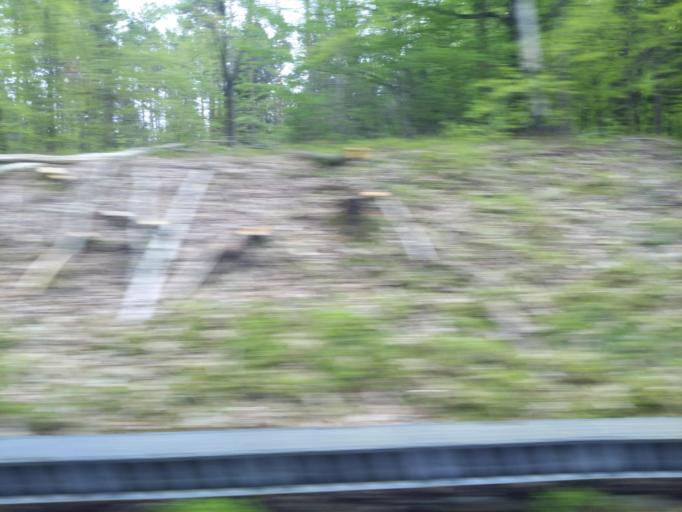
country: DE
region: Saxony
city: Bischofswerda
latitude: 51.1369
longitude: 14.2075
